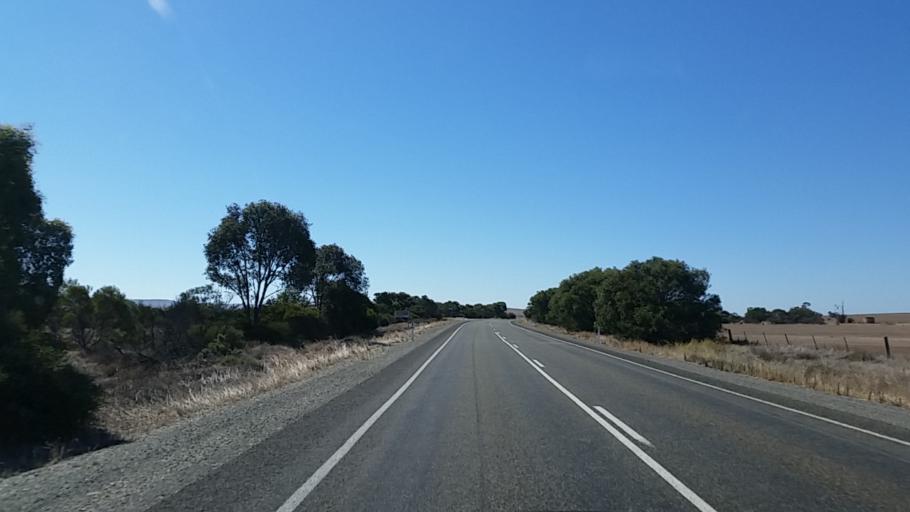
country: AU
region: South Australia
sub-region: Northern Areas
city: Jamestown
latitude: -33.2448
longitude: 138.8742
